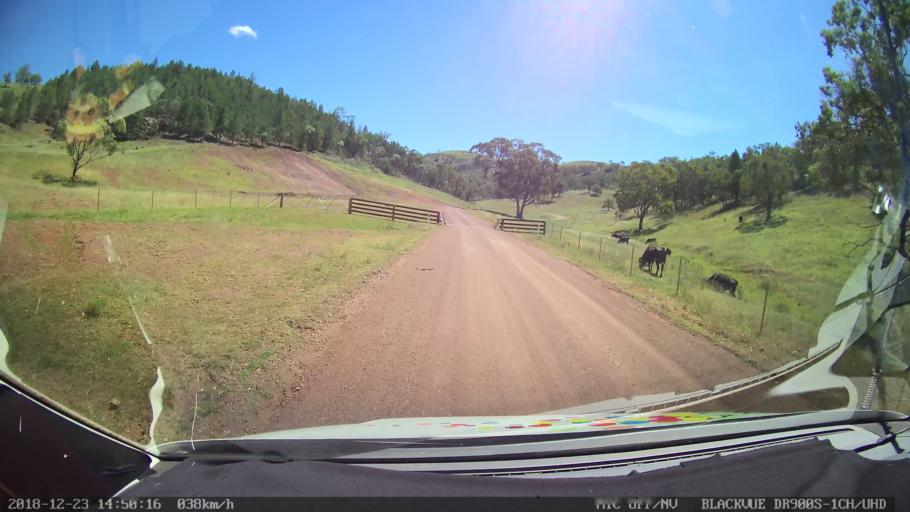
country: AU
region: New South Wales
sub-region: Tamworth Municipality
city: Manilla
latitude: -30.6715
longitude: 150.8581
